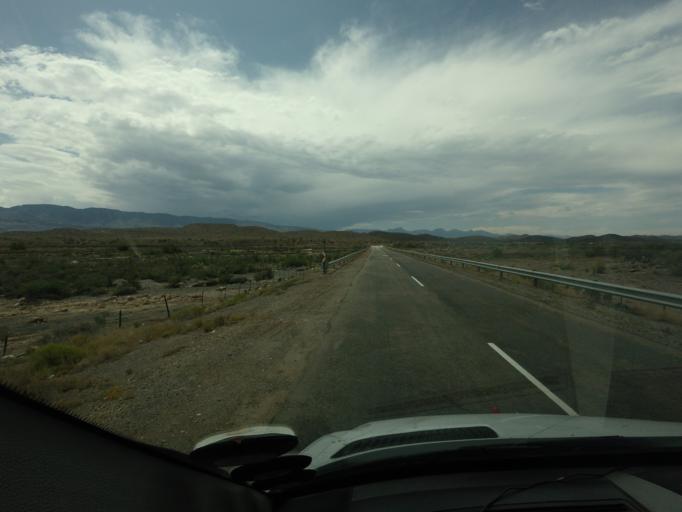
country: ZA
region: Western Cape
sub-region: Eden District Municipality
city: Ladismith
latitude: -33.6531
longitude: 21.0142
